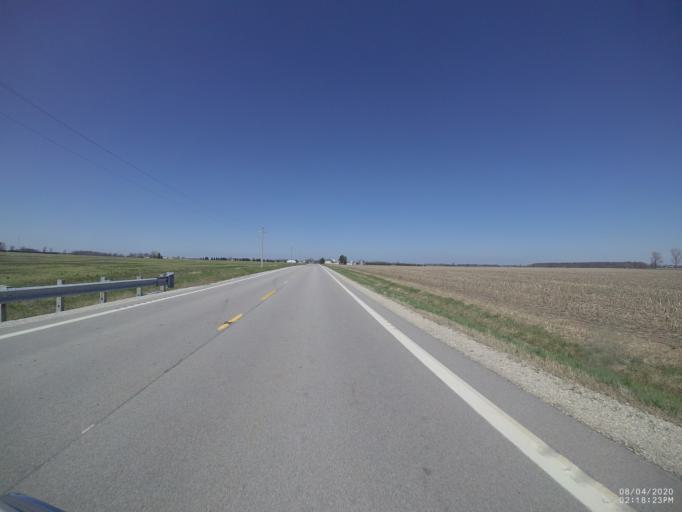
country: US
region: Ohio
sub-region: Sandusky County
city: Stony Prairie
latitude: 41.2844
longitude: -83.2354
